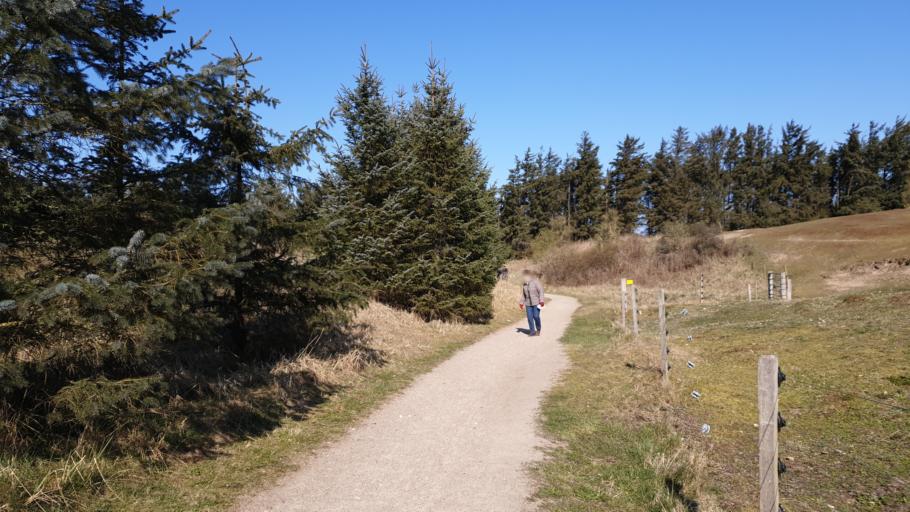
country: DK
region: North Denmark
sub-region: Hjorring Kommune
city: Hjorring
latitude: 57.4957
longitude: 9.8530
